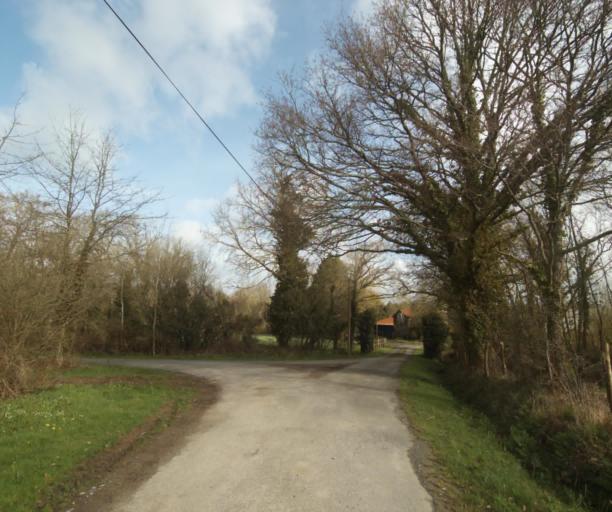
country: FR
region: Pays de la Loire
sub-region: Departement de la Loire-Atlantique
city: Bouvron
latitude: 47.4126
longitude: -1.8650
